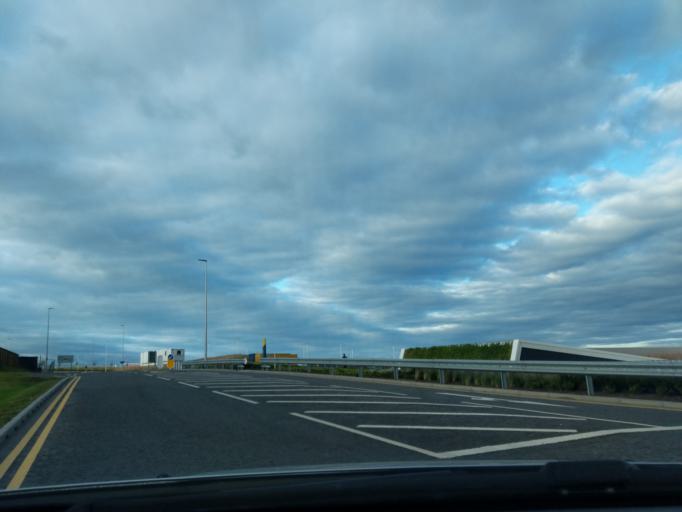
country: GB
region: Scotland
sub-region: Aberdeen City
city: Dyce
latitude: 57.1876
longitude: -2.1939
